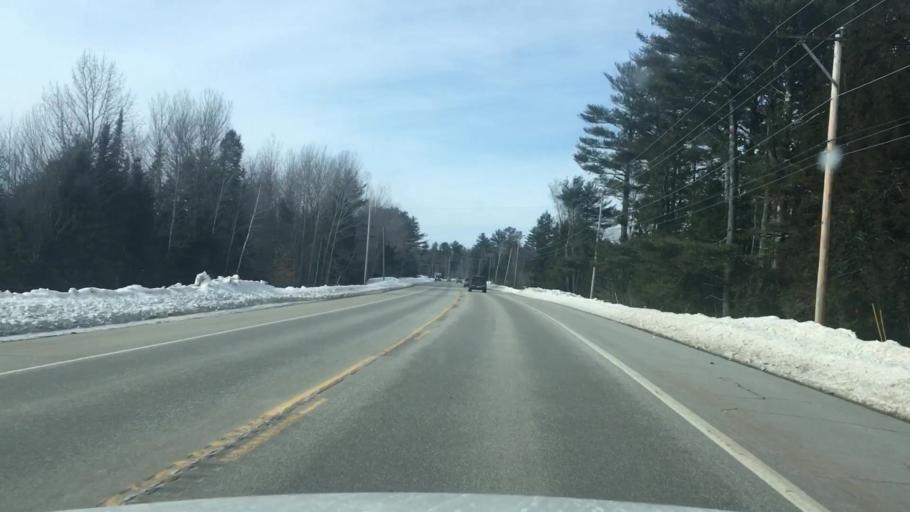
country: US
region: Maine
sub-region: Penobscot County
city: Kenduskeag
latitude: 44.9595
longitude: -68.9552
